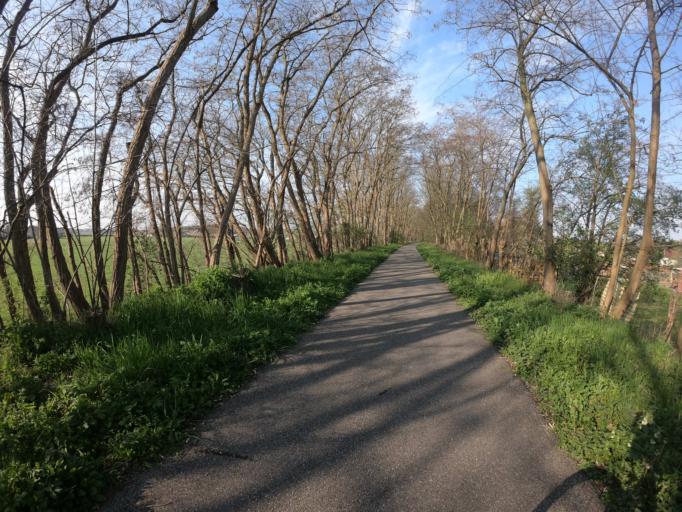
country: NL
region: Limburg
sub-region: Gemeente Stein
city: Berg
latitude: 51.0546
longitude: 5.7097
